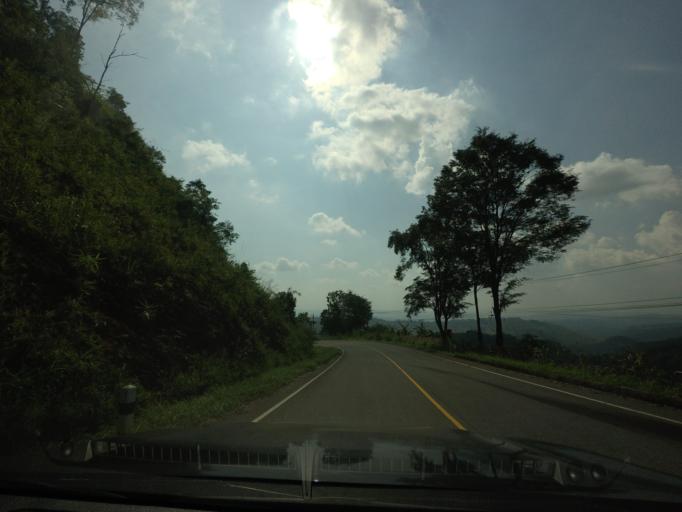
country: TH
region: Nan
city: Santi Suk
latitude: 18.9810
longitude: 100.9947
